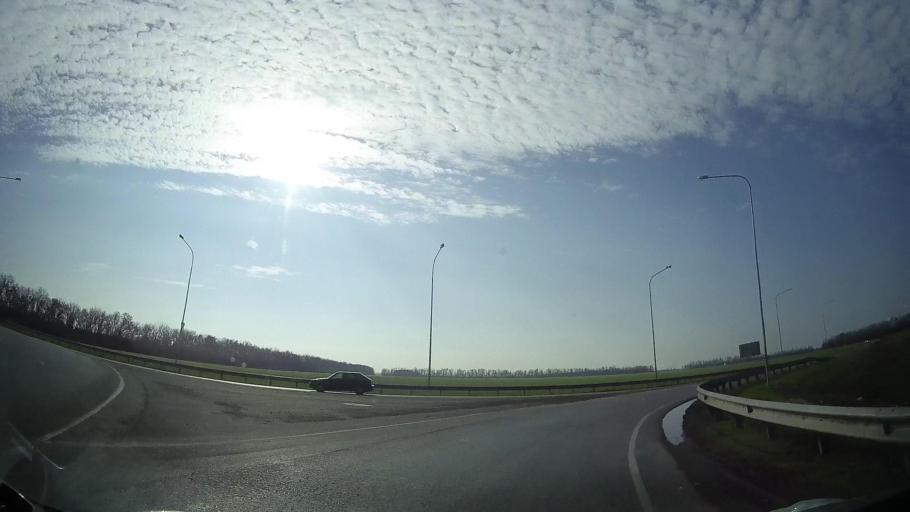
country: RU
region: Rostov
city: Tselina
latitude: 46.5263
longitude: 41.0791
